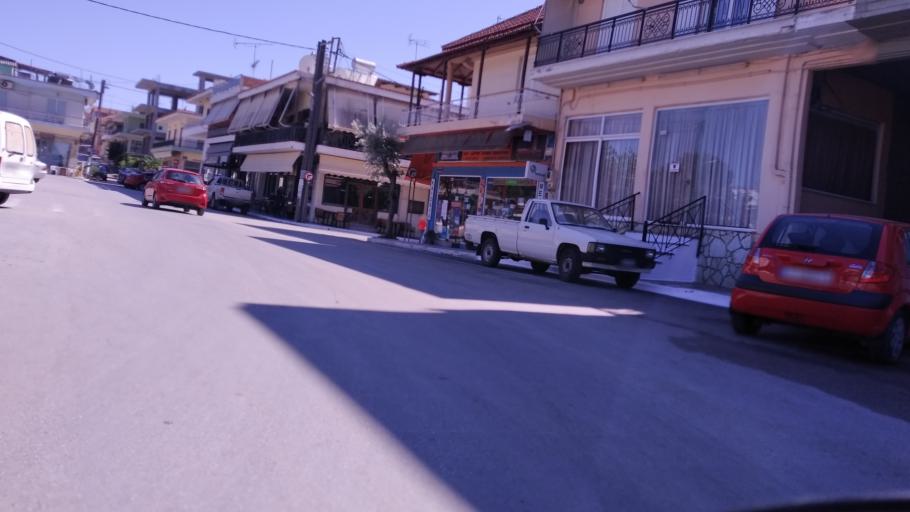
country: GR
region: Central Greece
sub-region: Nomos Fthiotidos
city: Malesina
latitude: 38.6233
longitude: 23.2306
